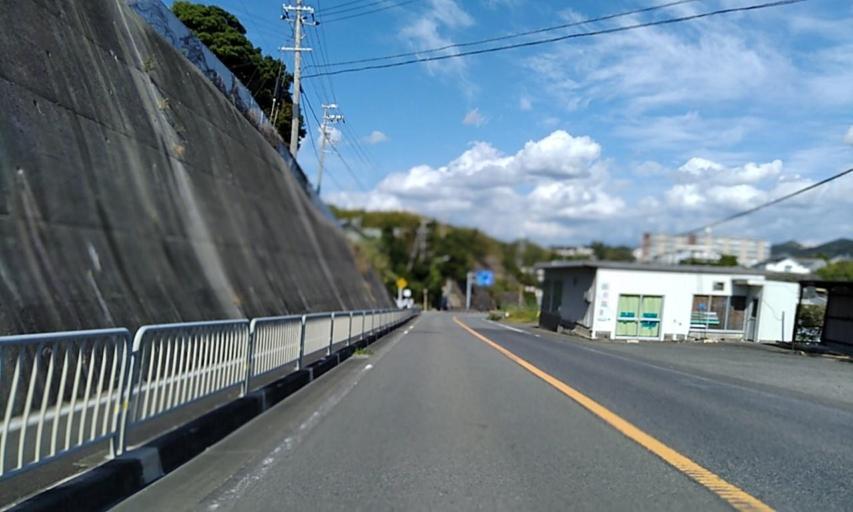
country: JP
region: Wakayama
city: Gobo
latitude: 33.8128
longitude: 135.2118
